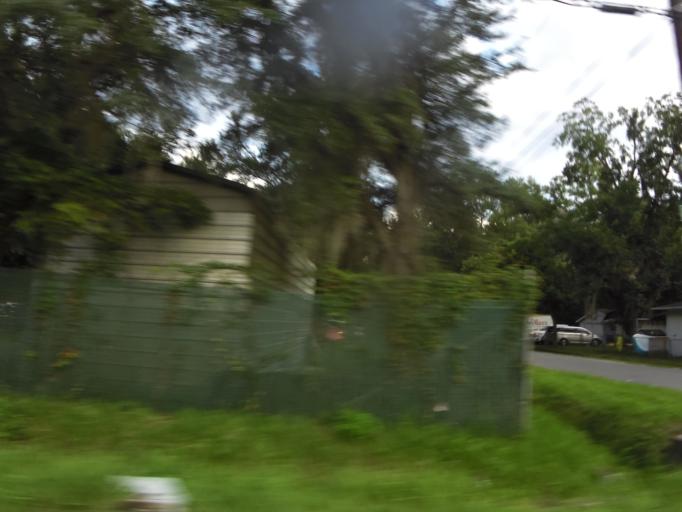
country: US
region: Florida
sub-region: Duval County
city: Jacksonville
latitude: 30.3195
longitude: -81.7751
